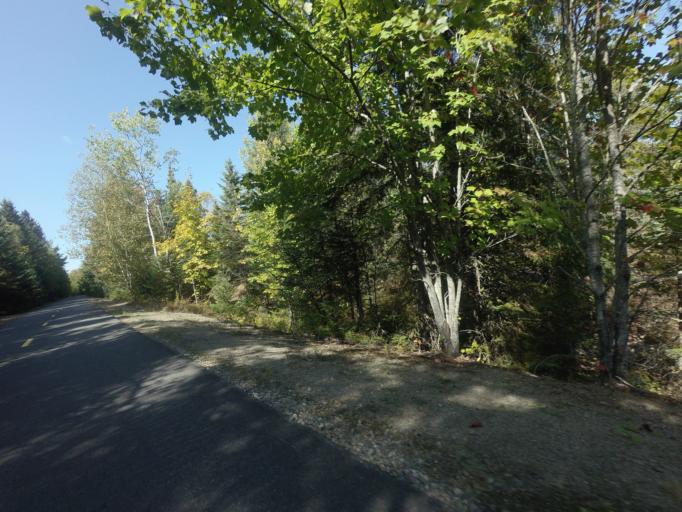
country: CA
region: Quebec
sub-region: Laurentides
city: Mont-Tremblant
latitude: 46.1247
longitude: -74.5257
